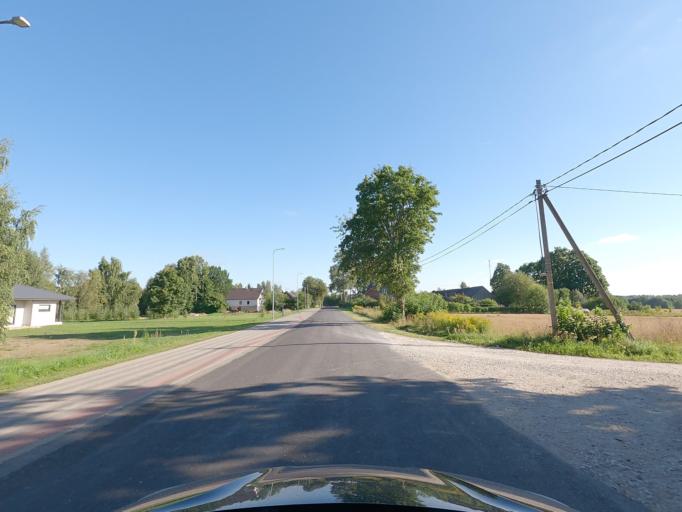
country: EE
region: Raplamaa
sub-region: Rapla vald
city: Rapla
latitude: 59.0124
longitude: 24.7856
